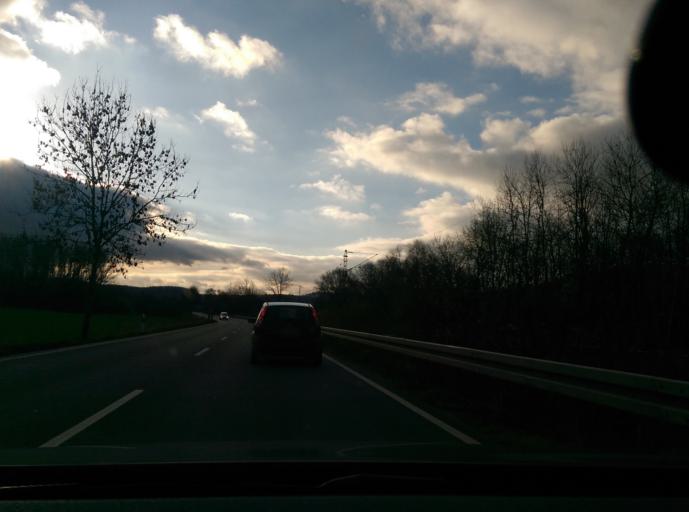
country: DE
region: Hesse
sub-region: Regierungsbezirk Kassel
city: Bad Sooden-Allendorf
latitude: 51.2778
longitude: 9.9637
